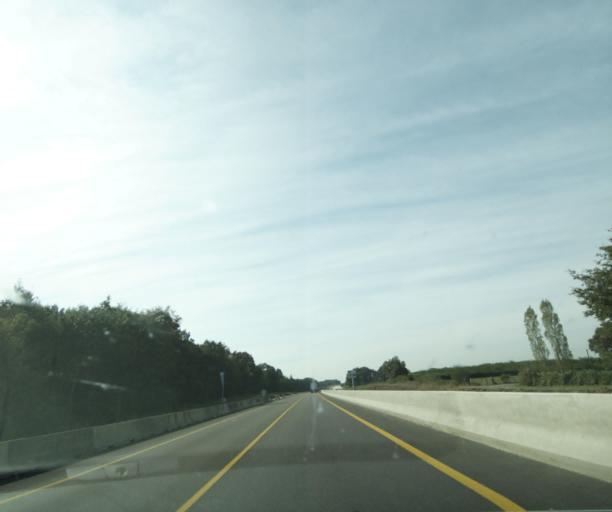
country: FR
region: Bourgogne
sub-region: Departement de Saone-et-Loire
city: Paray-le-Monial
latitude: 46.4934
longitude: 4.1564
